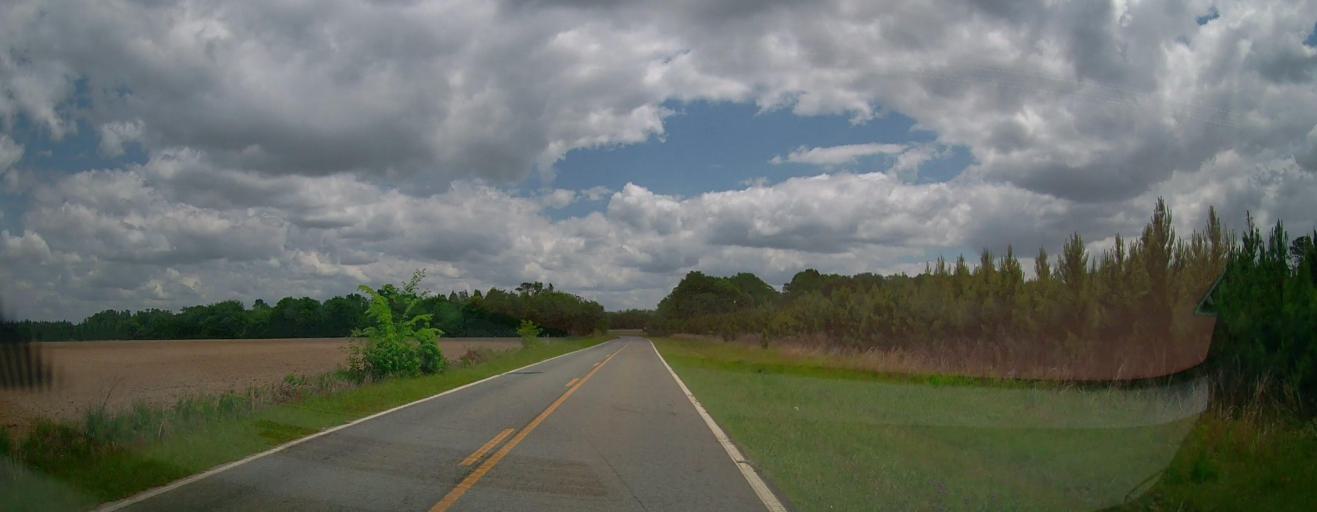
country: US
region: Georgia
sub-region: Laurens County
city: Dublin
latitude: 32.6030
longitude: -82.9809
